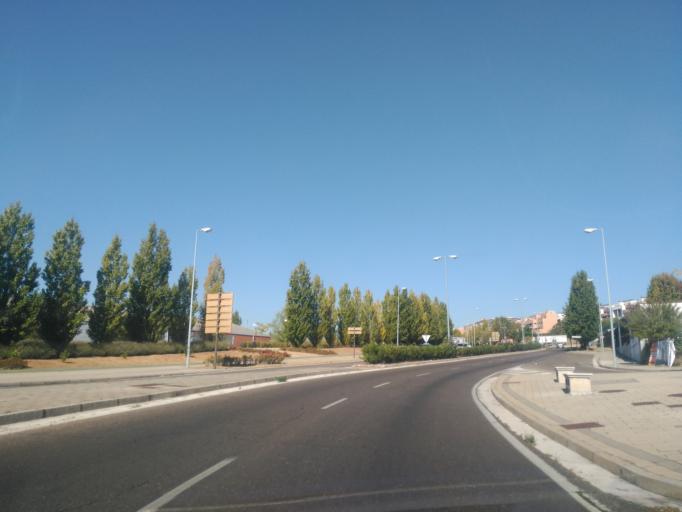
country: ES
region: Castille and Leon
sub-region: Provincia de Valladolid
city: Zaratan
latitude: 41.6282
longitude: -4.7592
